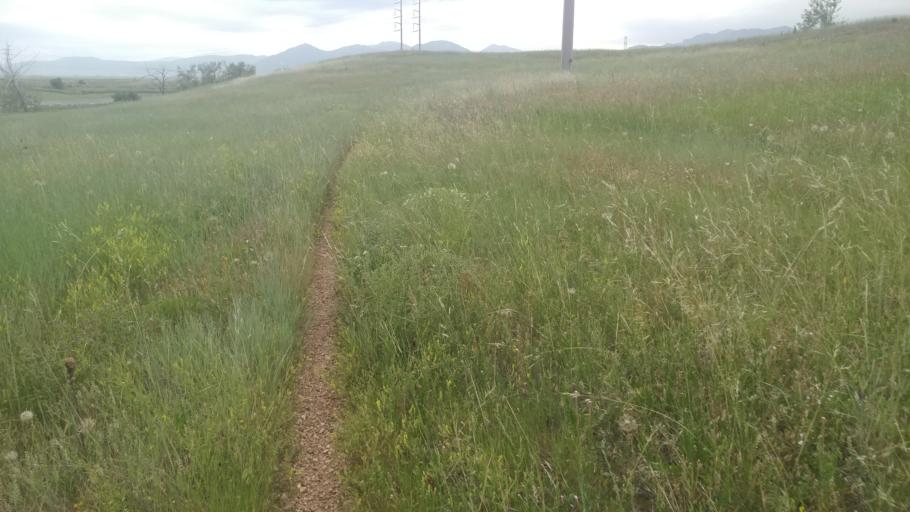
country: US
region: Colorado
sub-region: Boulder County
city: Superior
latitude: 39.9668
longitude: -105.1792
